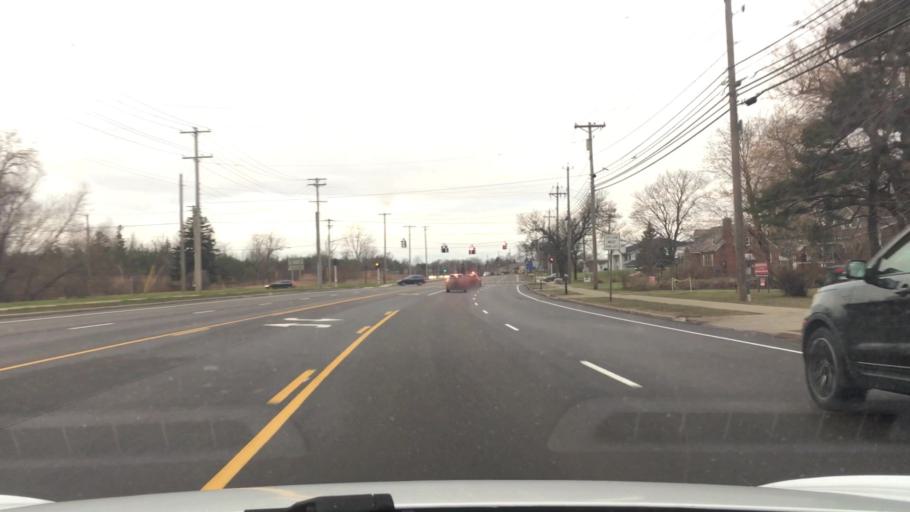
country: US
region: New York
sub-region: Erie County
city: Williamsville
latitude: 42.9778
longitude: -78.7232
